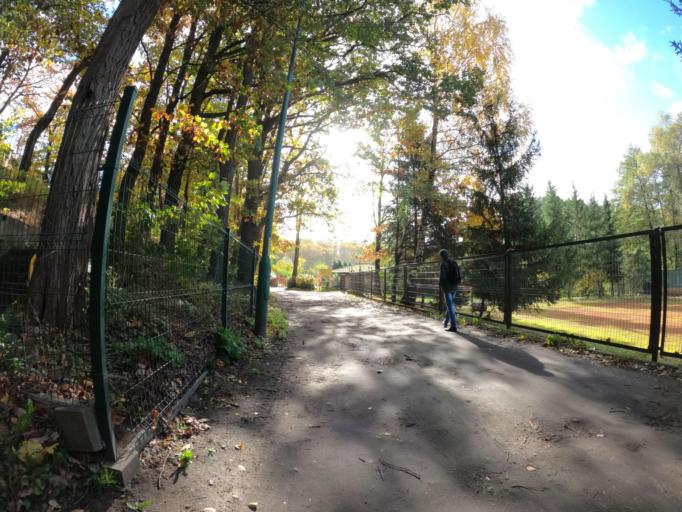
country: PL
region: West Pomeranian Voivodeship
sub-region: Powiat mysliborski
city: Barlinek
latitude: 52.9792
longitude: 15.2260
